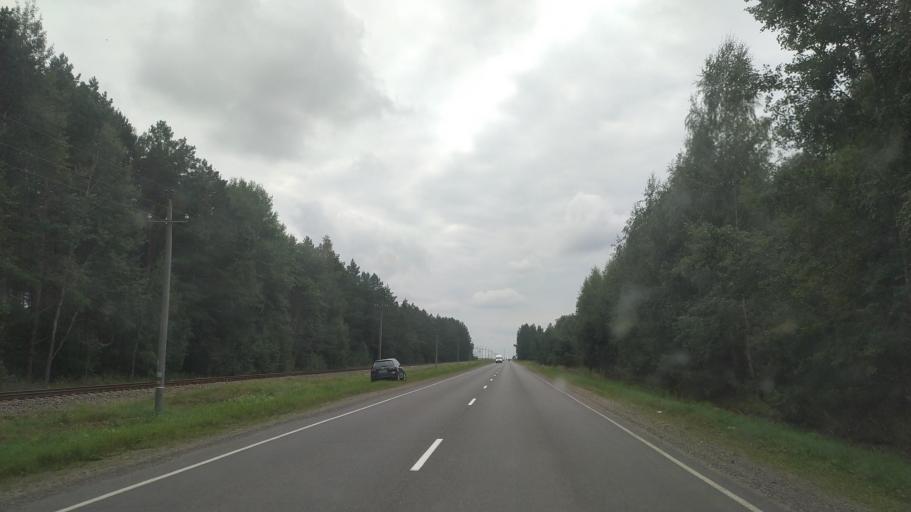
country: BY
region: Brest
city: Byelaazyorsk
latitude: 52.5272
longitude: 25.1463
